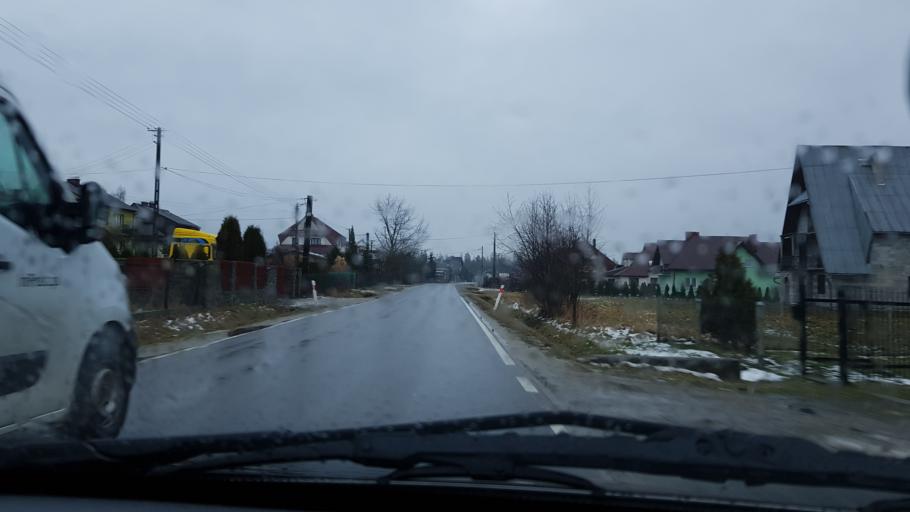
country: PL
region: Lesser Poland Voivodeship
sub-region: Powiat nowotarski
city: Lasek
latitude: 49.4895
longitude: 19.9686
